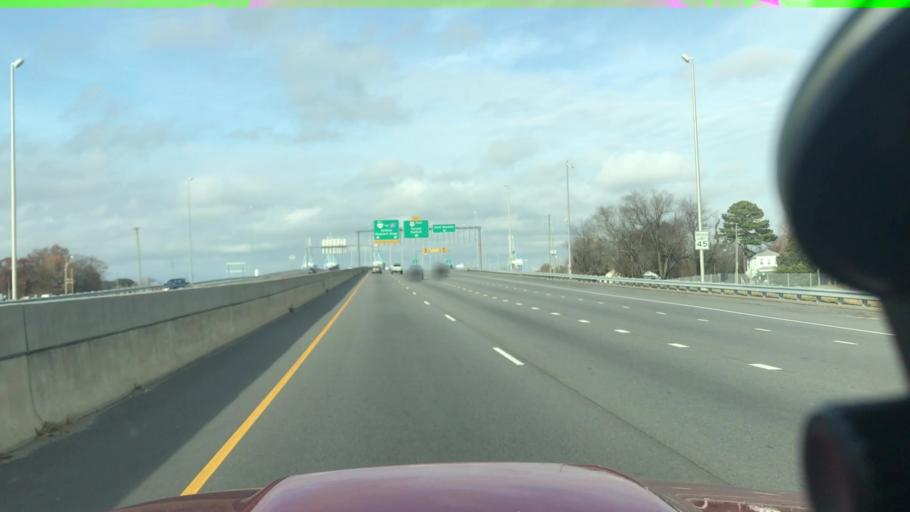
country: US
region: Virginia
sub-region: City of Portsmouth
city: Portsmouth
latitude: 36.8432
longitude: -76.3293
